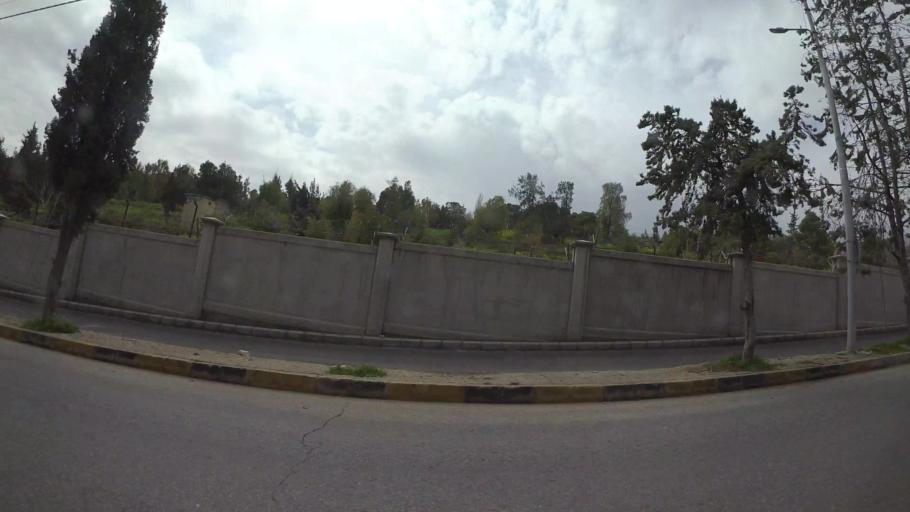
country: JO
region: Amman
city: Amman
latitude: 31.9608
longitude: 35.9508
